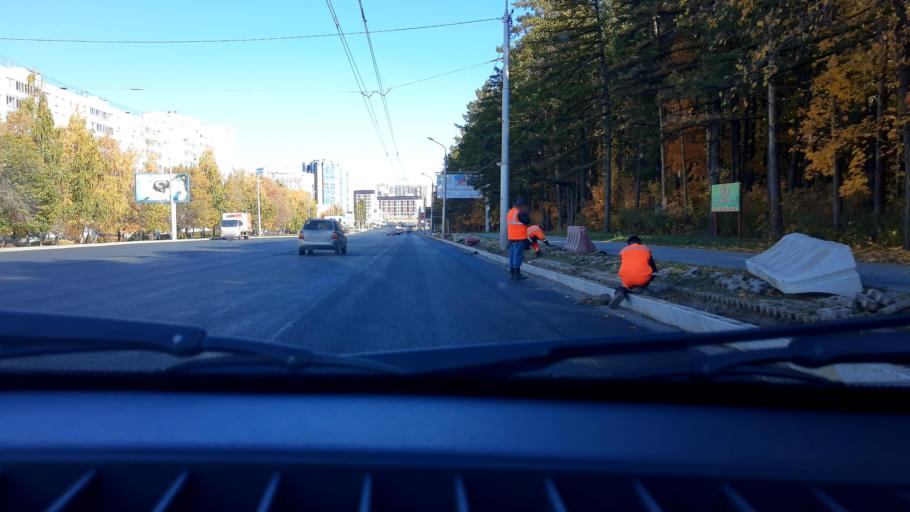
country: RU
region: Bashkortostan
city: Ufa
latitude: 54.7465
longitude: 56.0303
